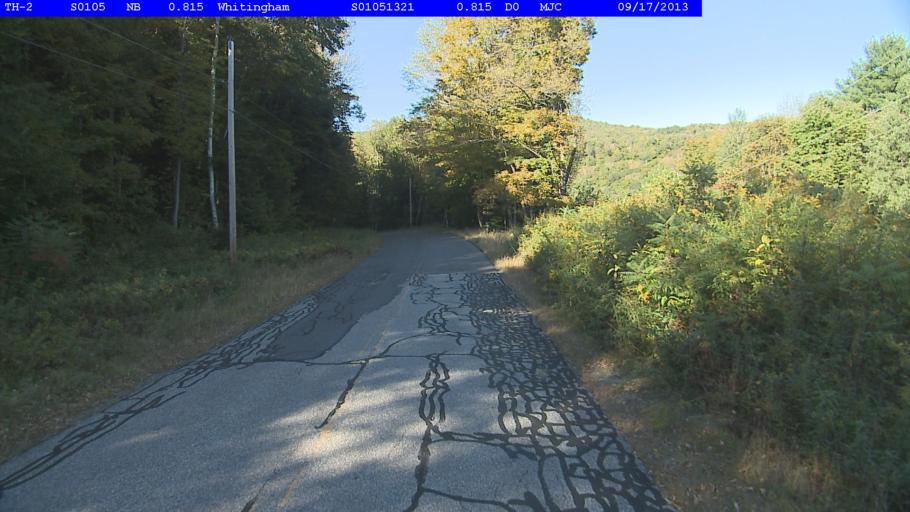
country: US
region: Massachusetts
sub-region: Franklin County
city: Charlemont
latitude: 42.7502
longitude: -72.9253
